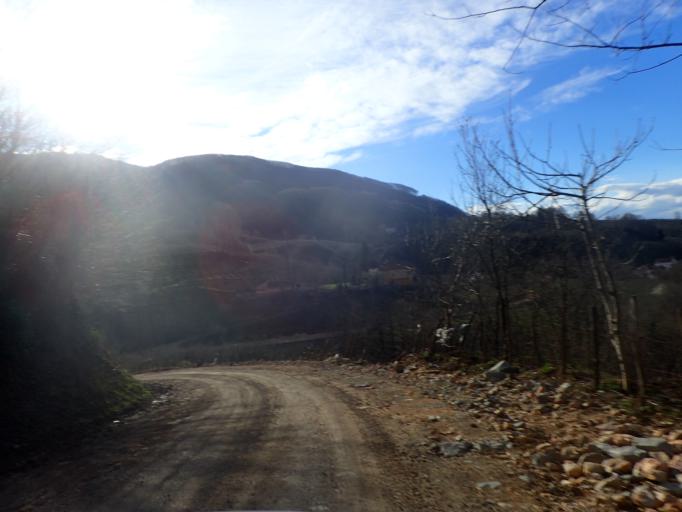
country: TR
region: Ordu
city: Kumru
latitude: 40.9292
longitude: 37.2440
